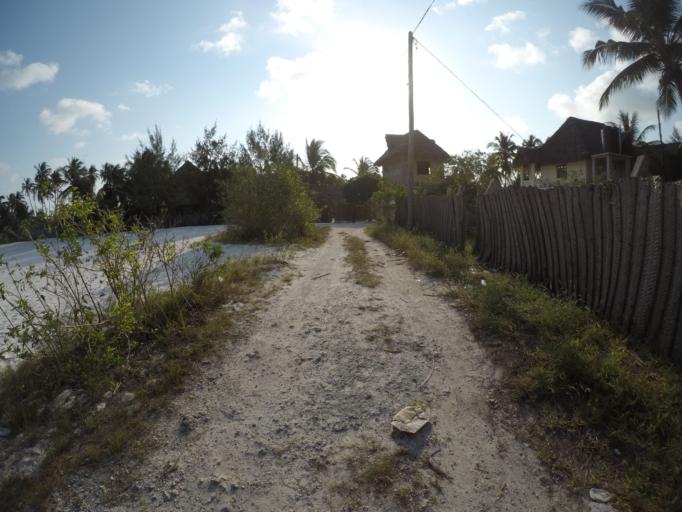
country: TZ
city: Kiwengwa
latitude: -6.1418
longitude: 39.4914
